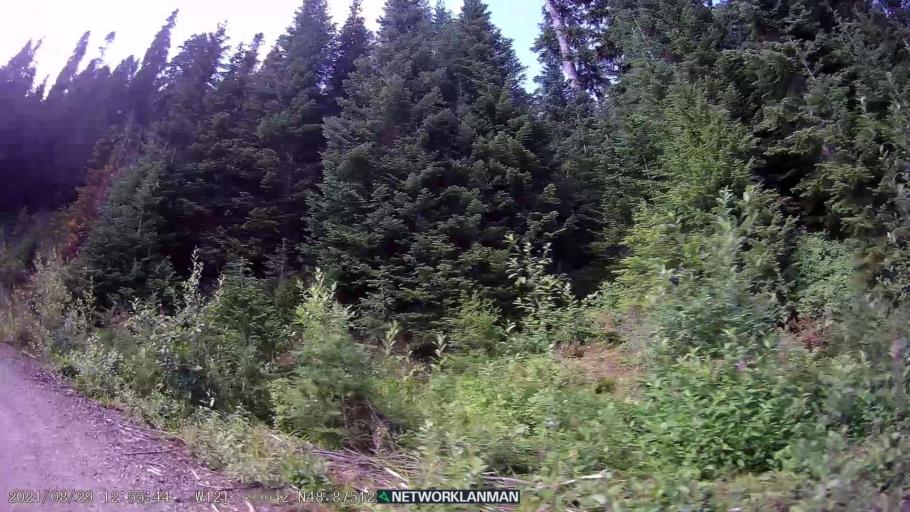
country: CA
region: British Columbia
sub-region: Fraser Valley Regional District
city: Chilliwack
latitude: 48.8752
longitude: -121.7998
